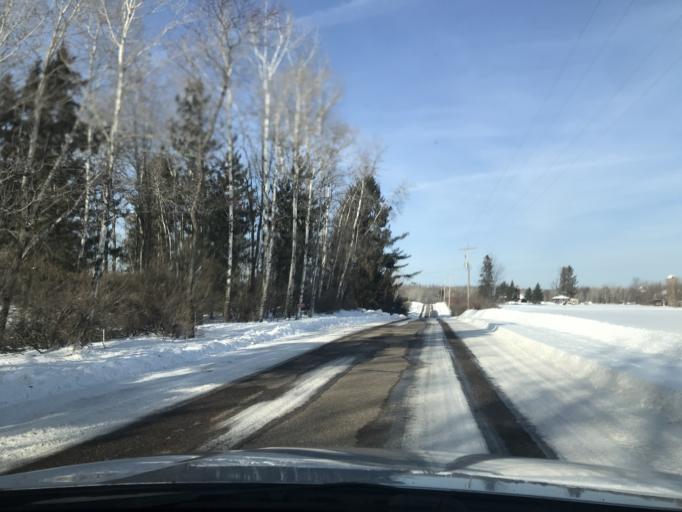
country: US
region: Wisconsin
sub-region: Menominee County
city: Legend Lake
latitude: 45.3117
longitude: -88.5218
